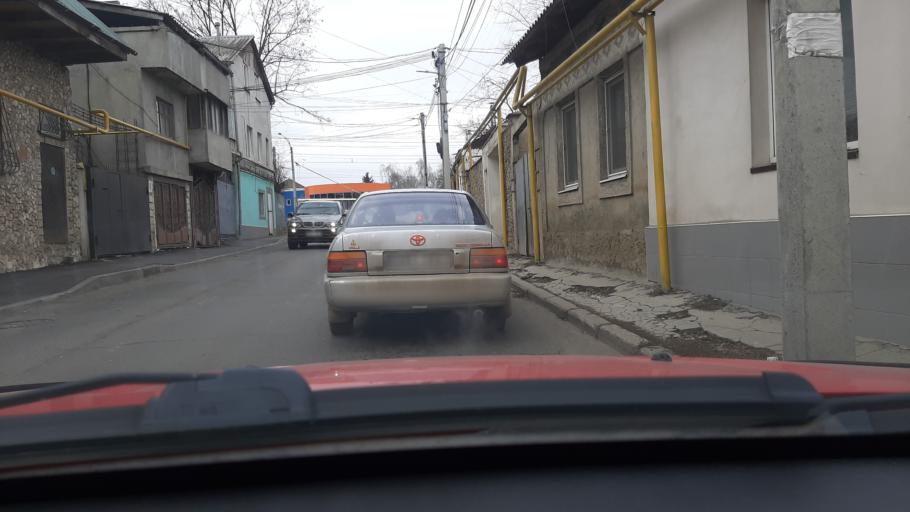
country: MD
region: Chisinau
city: Chisinau
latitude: 47.0094
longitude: 28.8378
